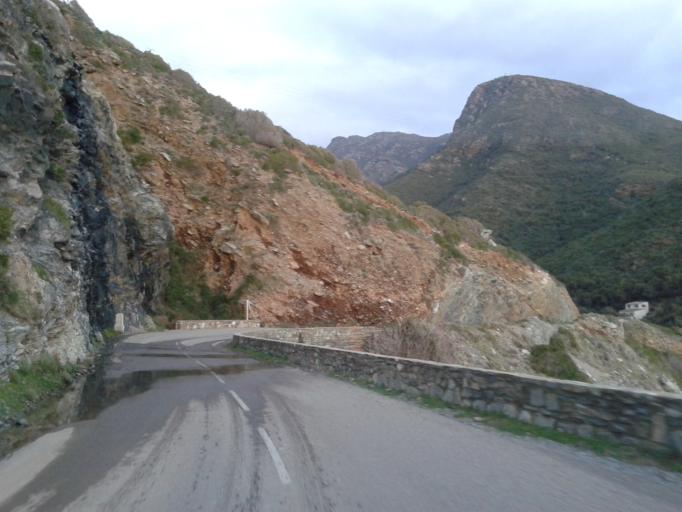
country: FR
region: Corsica
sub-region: Departement de la Haute-Corse
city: Saint-Florent
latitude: 42.7620
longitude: 9.3389
